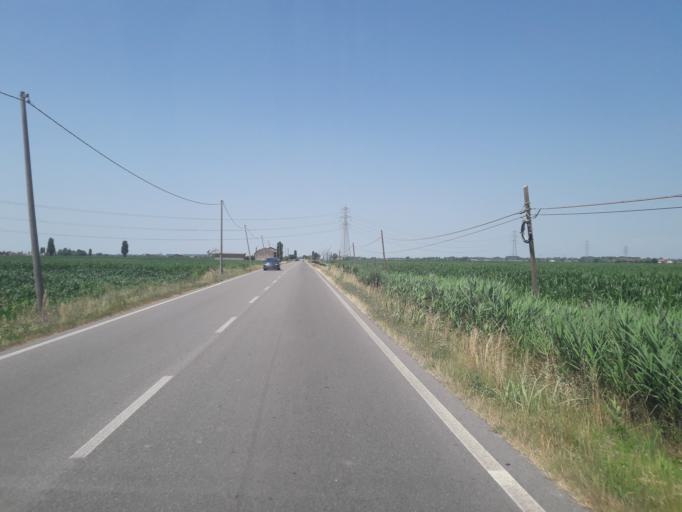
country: IT
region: Veneto
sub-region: Provincia di Rovigo
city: Papozze
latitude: 45.0051
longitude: 12.1771
